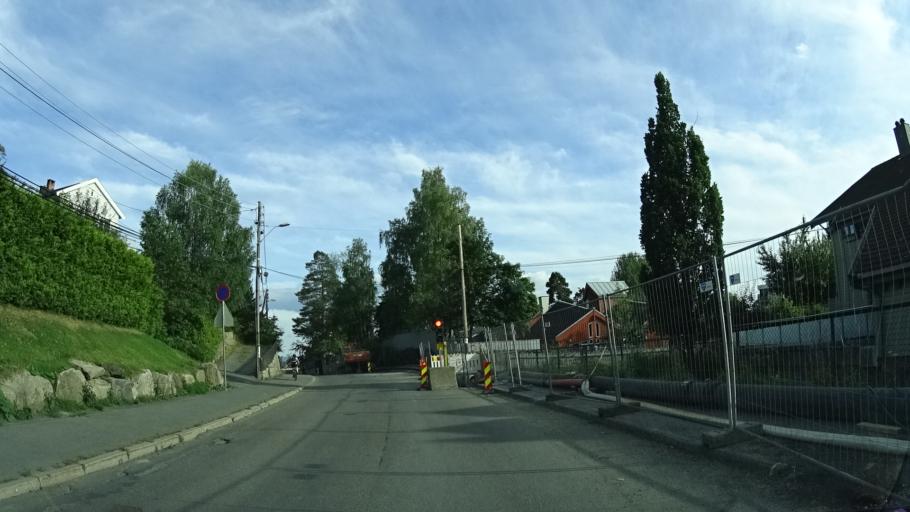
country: NO
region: Oslo
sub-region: Oslo
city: Sjolyststranda
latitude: 59.9538
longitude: 10.6581
